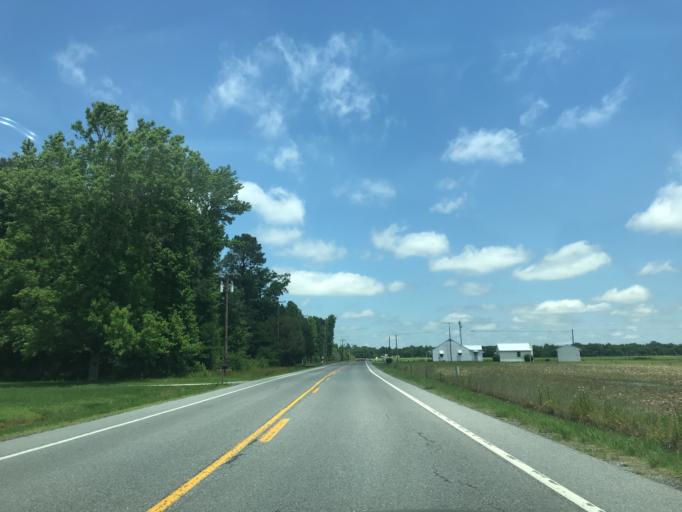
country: US
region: Maryland
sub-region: Caroline County
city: Federalsburg
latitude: 38.7231
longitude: -75.7349
